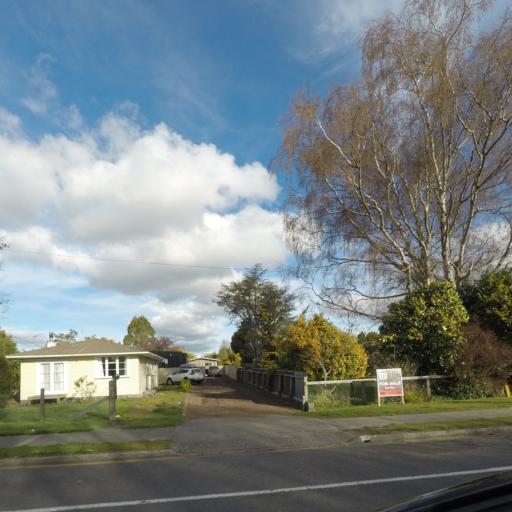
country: NZ
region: Manawatu-Wanganui
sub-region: Ruapehu District
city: Waiouru
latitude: -39.4112
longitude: 175.4060
